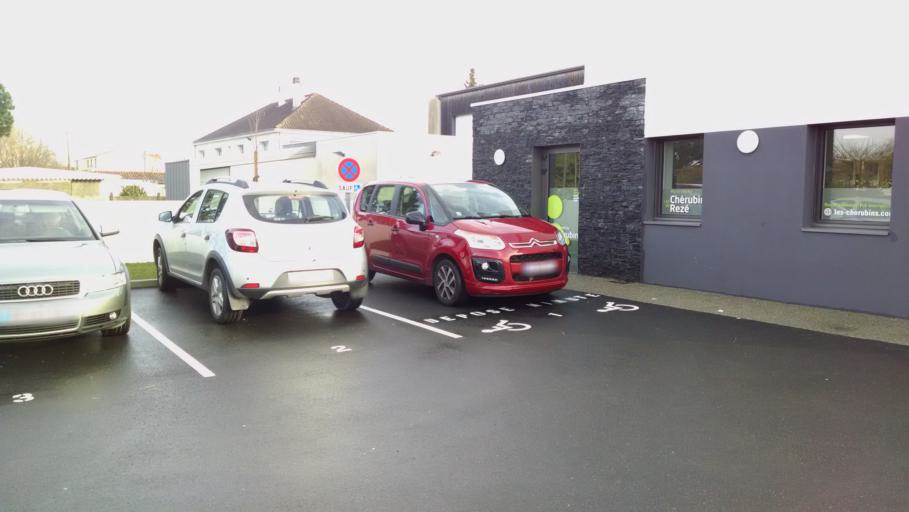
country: FR
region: Pays de la Loire
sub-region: Departement de la Loire-Atlantique
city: Reze
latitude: 47.1735
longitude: -1.5442
